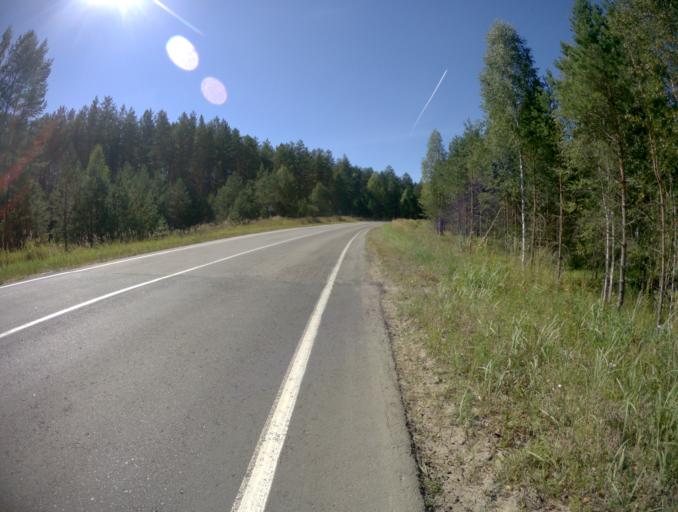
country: RU
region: Vladimir
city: Zolotkovo
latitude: 55.6255
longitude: 40.9002
